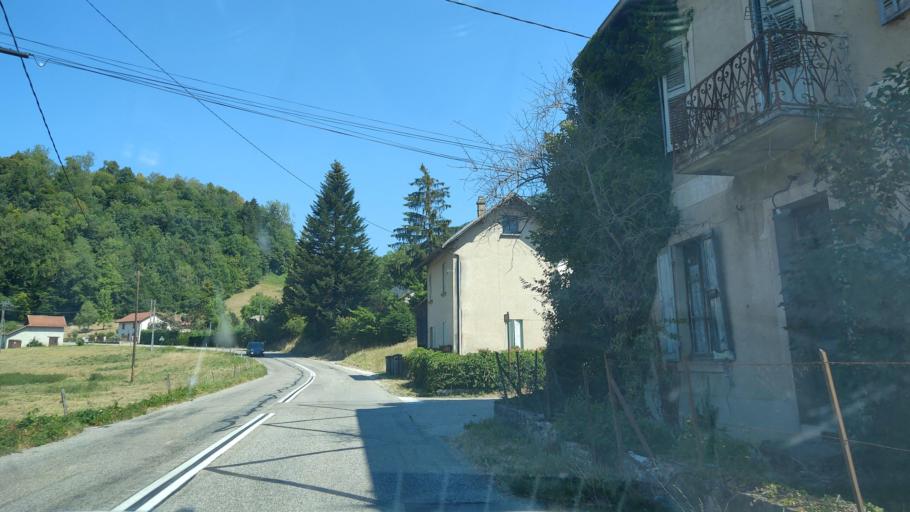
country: FR
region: Rhone-Alpes
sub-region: Departement de la Savoie
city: Novalaise
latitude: 45.5839
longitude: 5.7932
